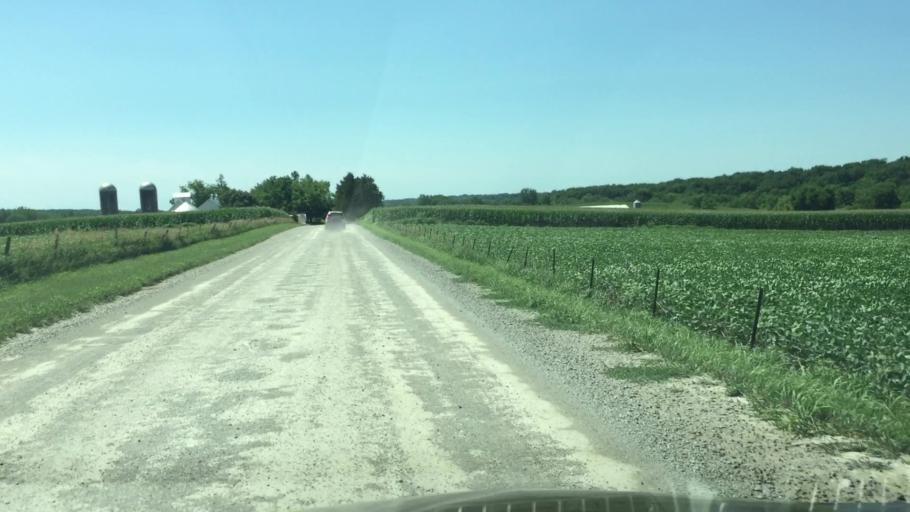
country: US
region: Iowa
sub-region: Linn County
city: Ely
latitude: 41.8266
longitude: -91.5899
